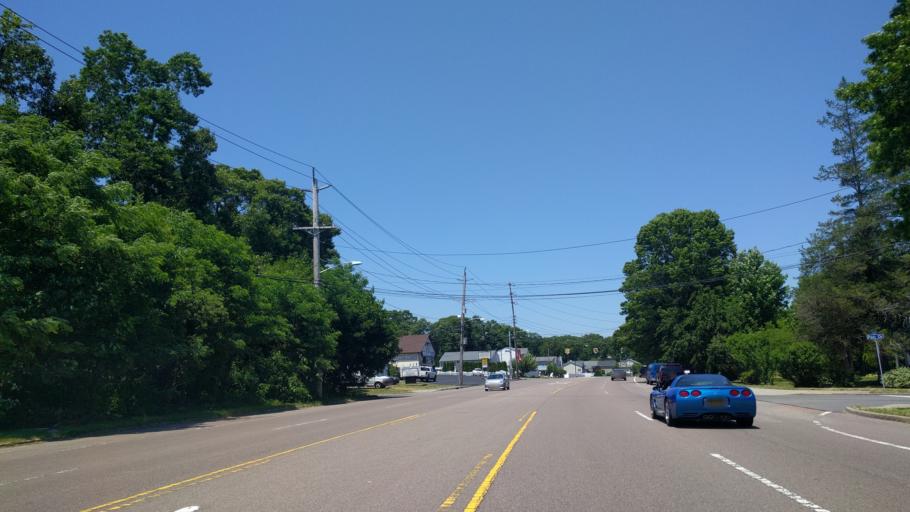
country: US
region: New York
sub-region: Suffolk County
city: Lake Ronkonkoma
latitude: 40.8258
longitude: -73.1326
